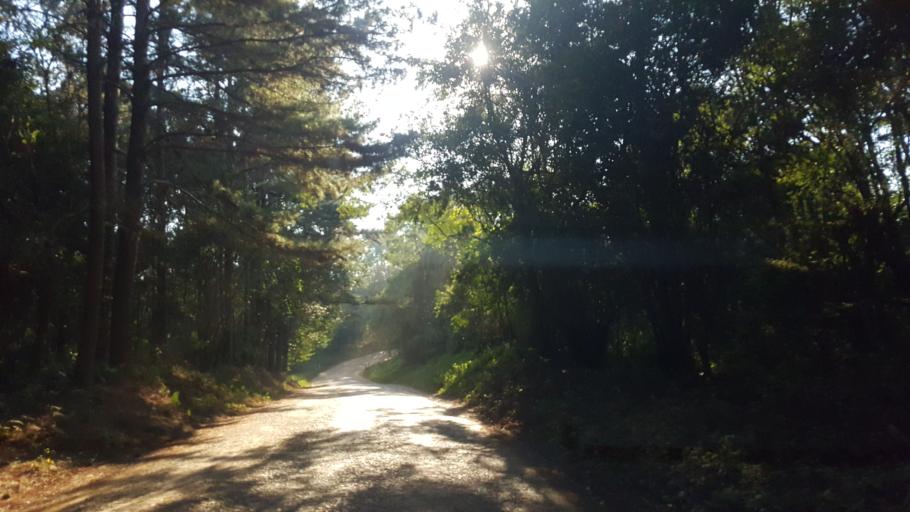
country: AR
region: Misiones
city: Capiovi
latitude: -26.8926
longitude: -55.0578
